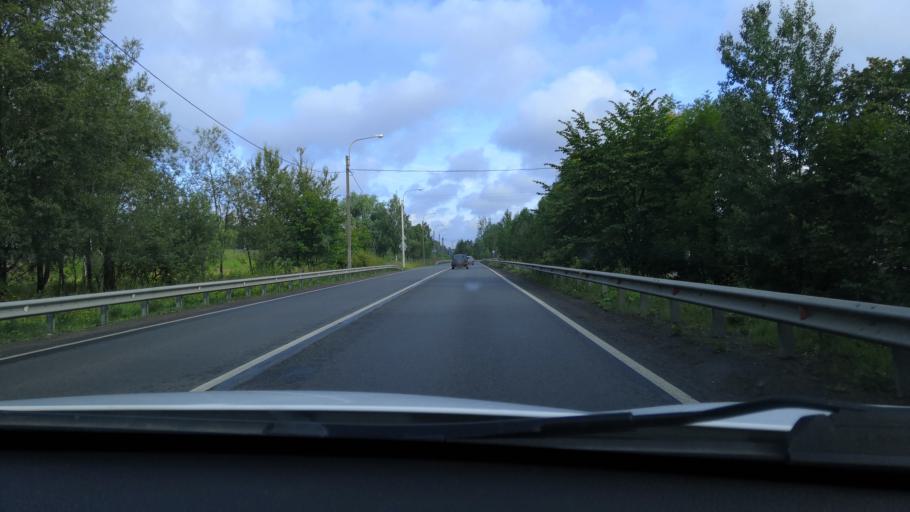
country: RU
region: St.-Petersburg
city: Tyarlevo
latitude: 59.7029
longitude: 30.4396
